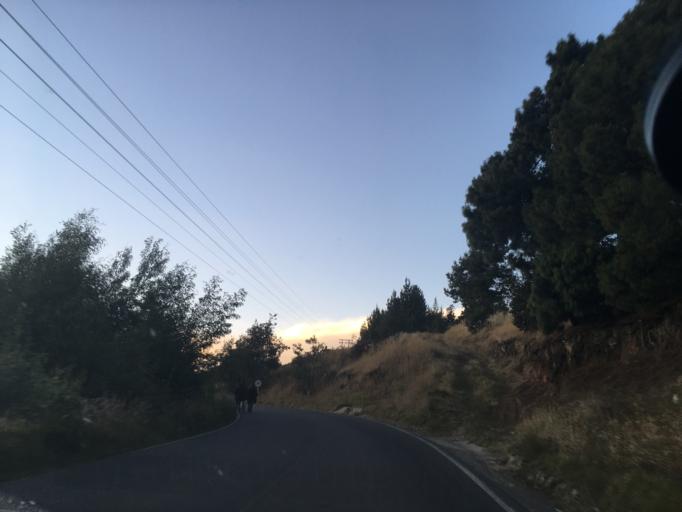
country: CO
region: Boyaca
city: Aquitania
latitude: 5.5881
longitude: -72.9011
